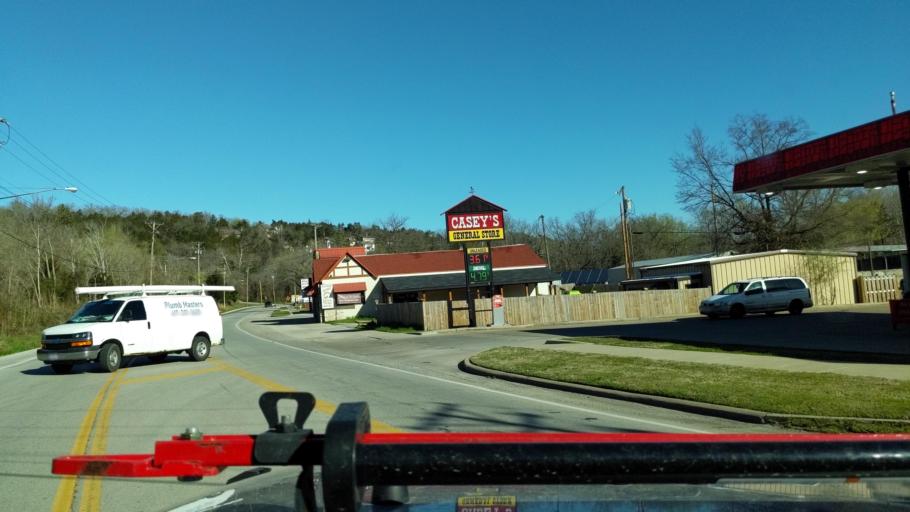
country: US
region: Missouri
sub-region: Taney County
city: Hollister
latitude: 36.6246
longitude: -93.2173
